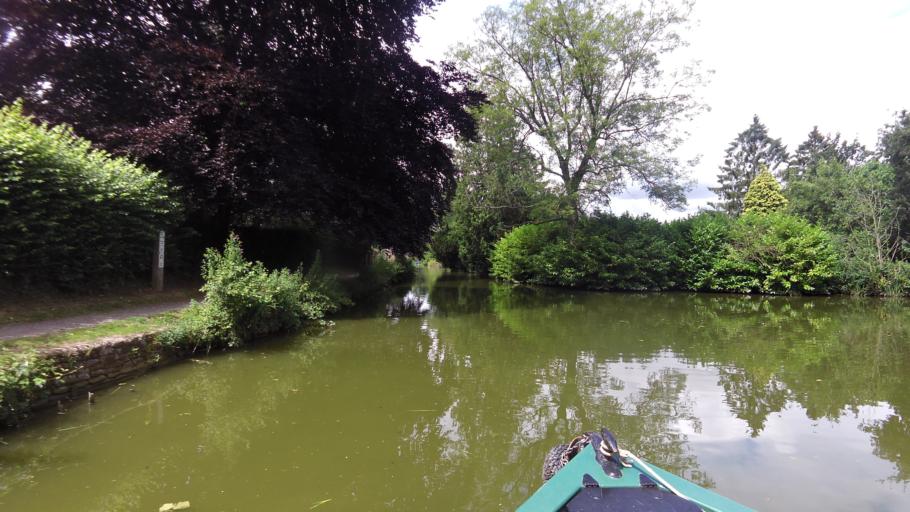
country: GB
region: England
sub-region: West Berkshire
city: Hungerford
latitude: 51.4161
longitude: -1.5122
